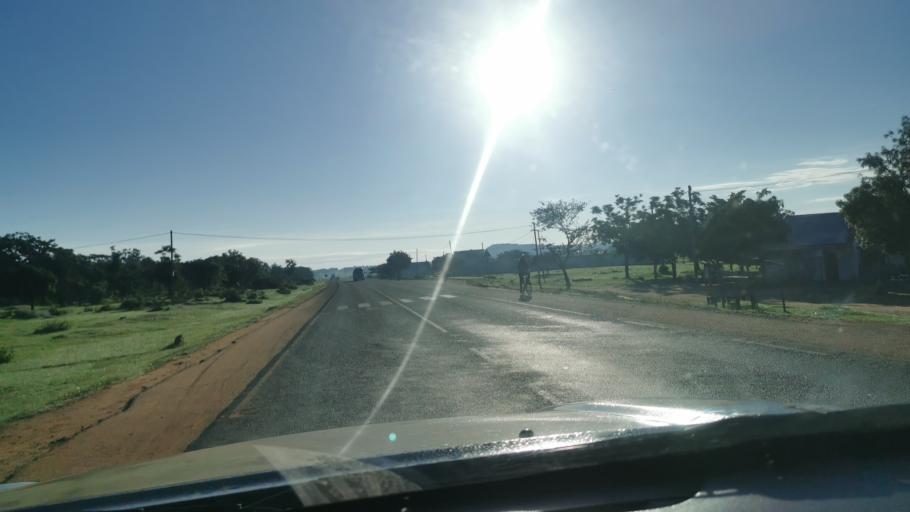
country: TZ
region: Shinyanga
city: Kahama
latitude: -3.8389
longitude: 32.6403
